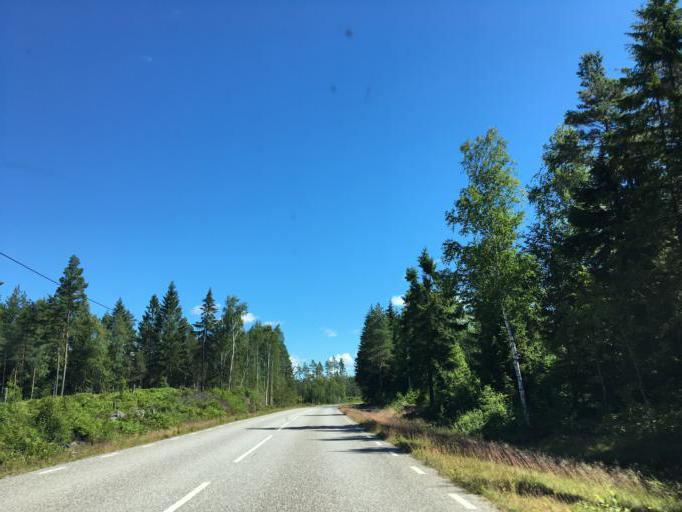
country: SE
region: OErebro
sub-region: Laxa Kommun
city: Laxa
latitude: 58.7860
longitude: 14.5517
